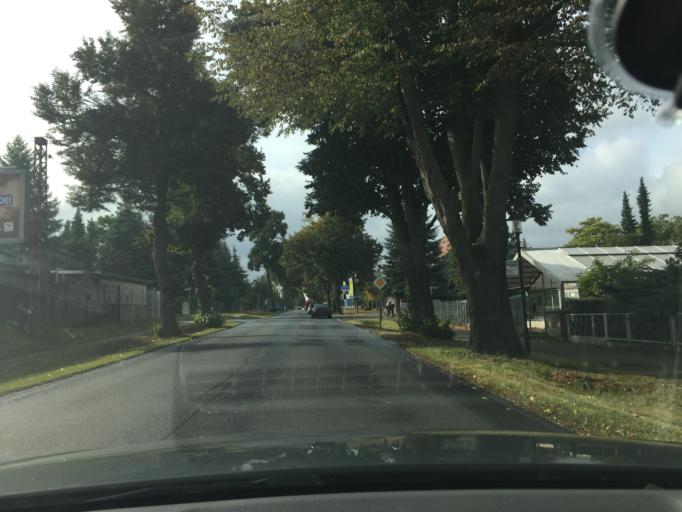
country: DE
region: Berlin
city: Hellersdorf
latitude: 52.5328
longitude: 13.6297
